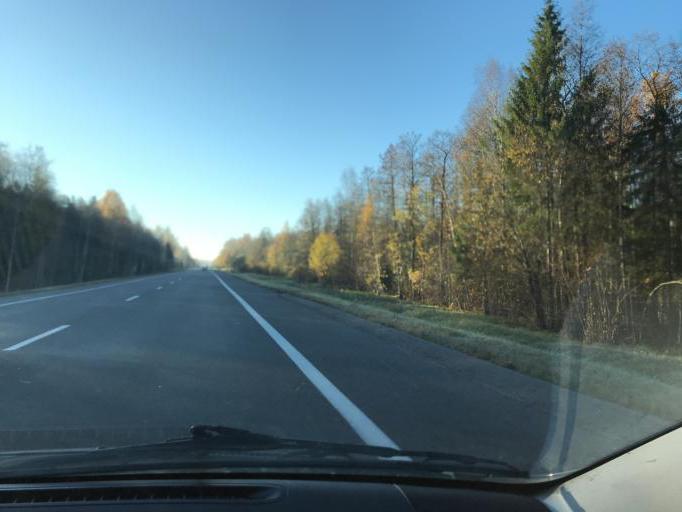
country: BY
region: Vitebsk
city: Vitebsk
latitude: 54.9850
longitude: 30.3442
